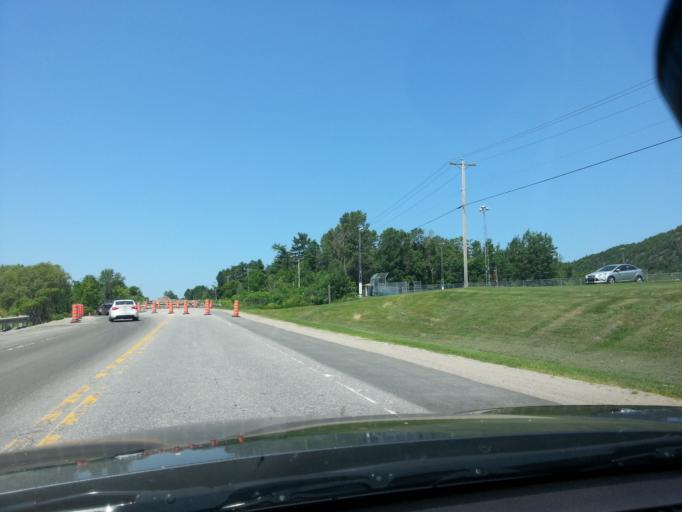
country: CA
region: Quebec
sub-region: Outaouais
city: Wakefield
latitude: 45.5443
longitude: -76.0536
